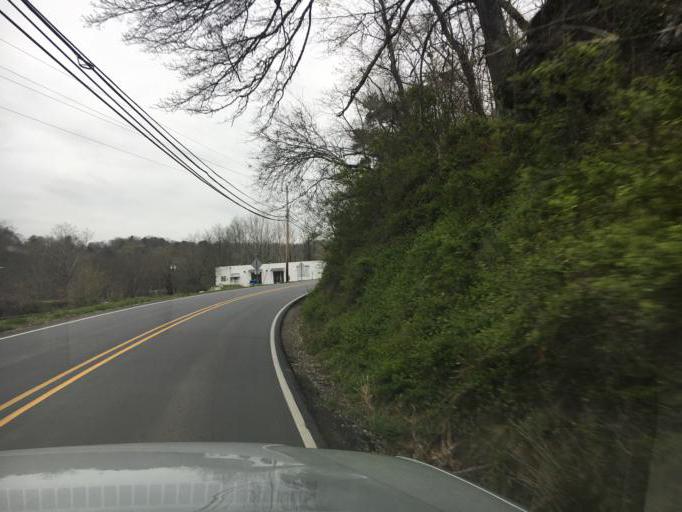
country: US
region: North Carolina
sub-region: Buncombe County
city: Woodfin
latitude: 35.6241
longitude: -82.5973
